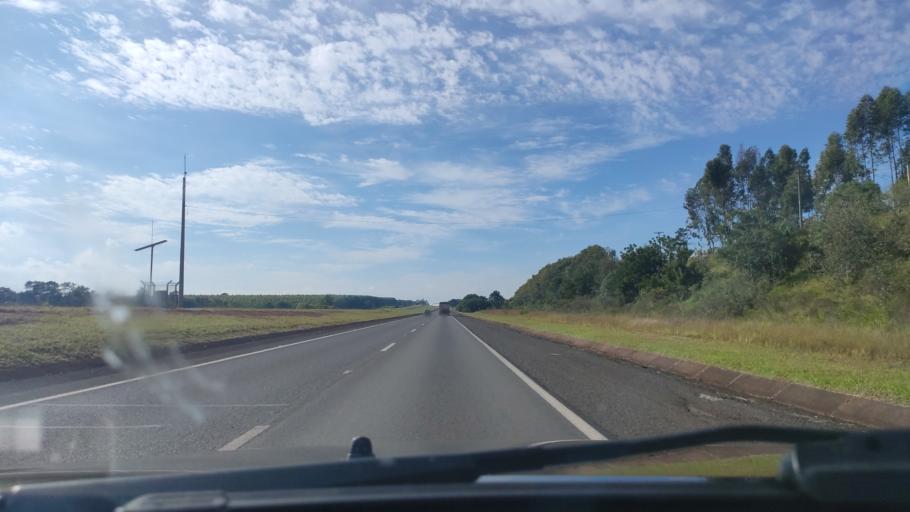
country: BR
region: Sao Paulo
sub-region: Itatinga
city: Itatinga
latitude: -23.0421
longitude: -48.6158
